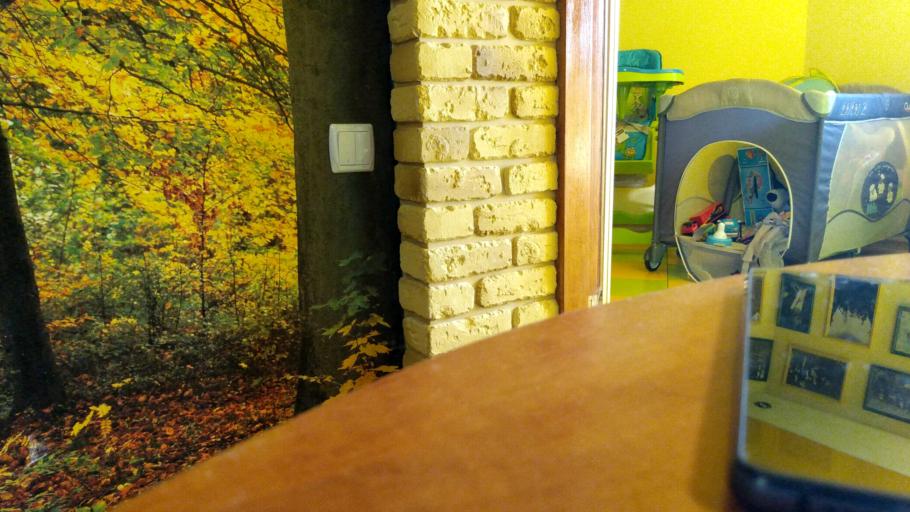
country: RU
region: Tverskaya
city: Kalashnikovo
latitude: 57.2962
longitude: 35.3450
